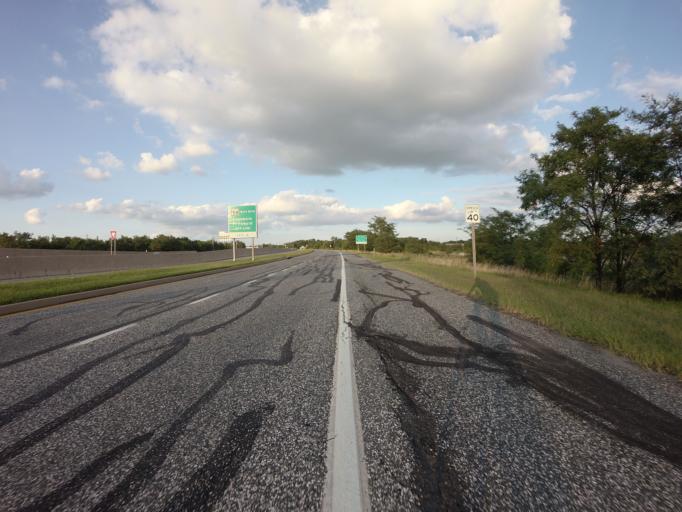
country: US
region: Maryland
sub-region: Baltimore County
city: Edgemere
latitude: 39.2364
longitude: -76.4696
